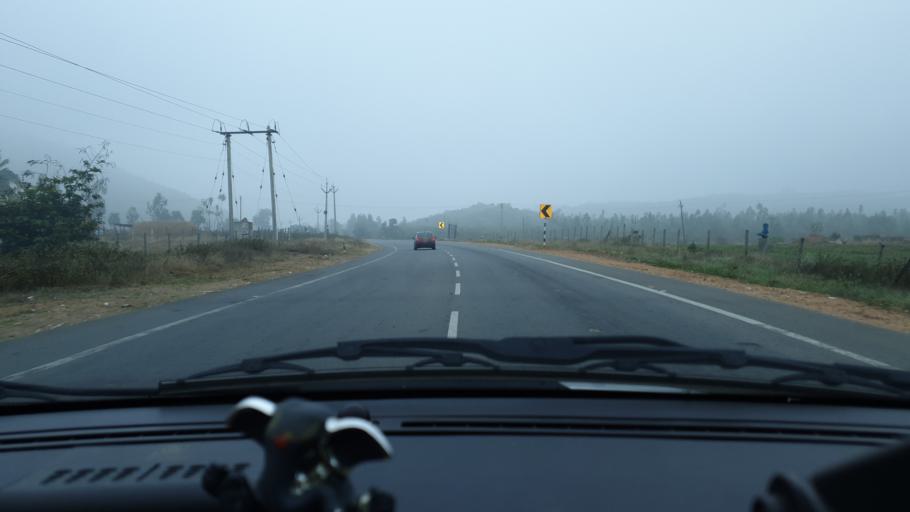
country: IN
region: Telangana
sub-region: Mahbubnagar
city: Farrukhnagar
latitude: 16.9136
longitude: 78.5271
